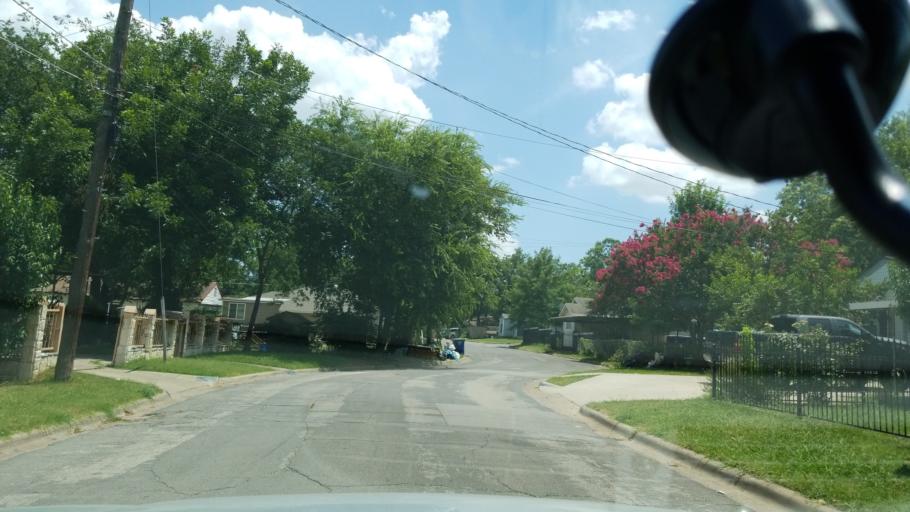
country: US
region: Texas
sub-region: Dallas County
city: Cockrell Hill
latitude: 32.7319
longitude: -96.8793
